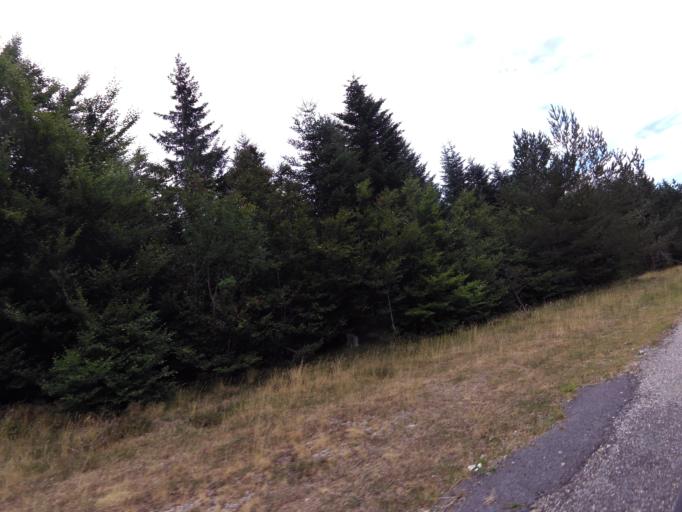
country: FR
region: Languedoc-Roussillon
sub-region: Departement du Gard
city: Valleraugue
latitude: 44.0830
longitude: 3.5682
